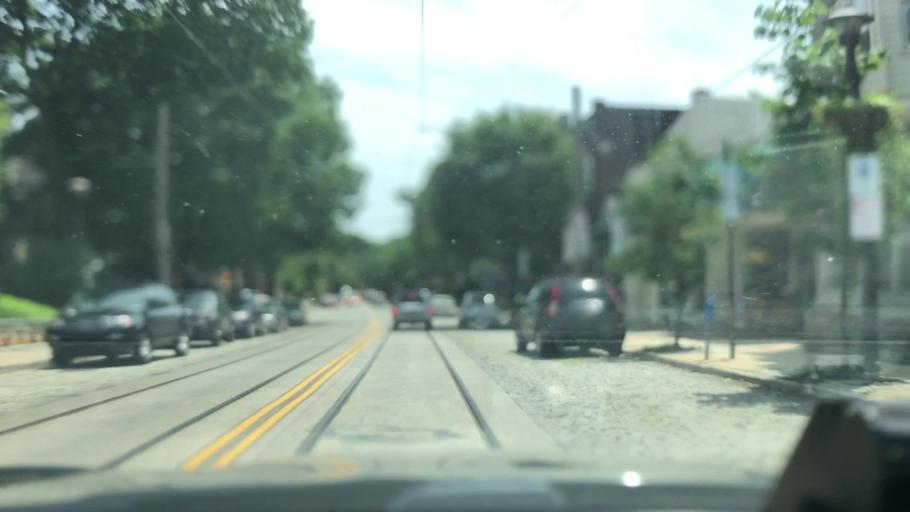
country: US
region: Pennsylvania
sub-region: Montgomery County
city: Wyndmoor
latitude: 40.0719
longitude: -75.2019
